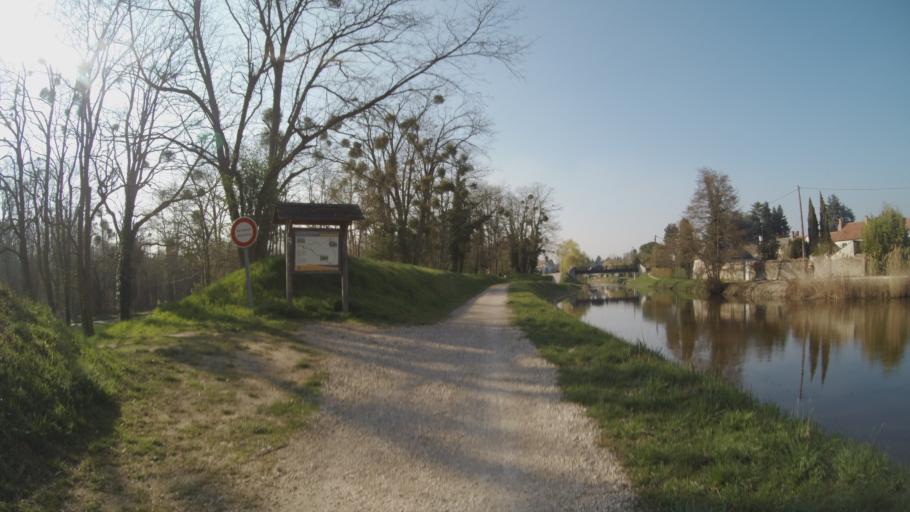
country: FR
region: Centre
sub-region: Departement du Loiret
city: Checy
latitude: 47.8944
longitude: 2.0024
